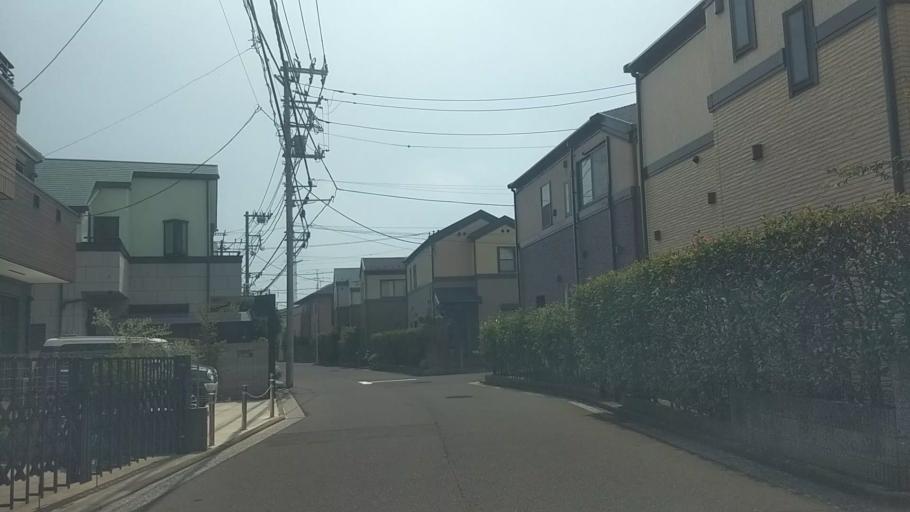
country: JP
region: Kanagawa
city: Yokohama
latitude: 35.5104
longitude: 139.6502
